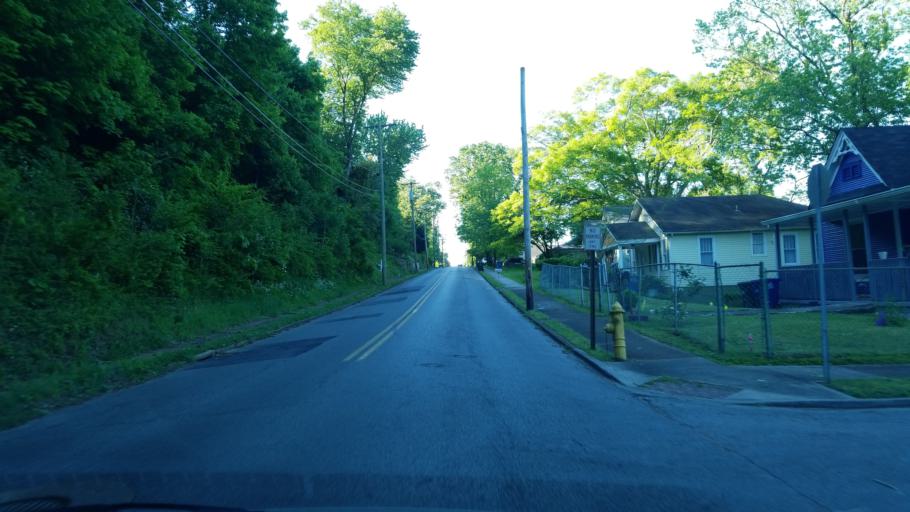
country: US
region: Tennessee
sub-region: Hamilton County
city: Lookout Mountain
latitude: 35.0050
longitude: -85.3275
